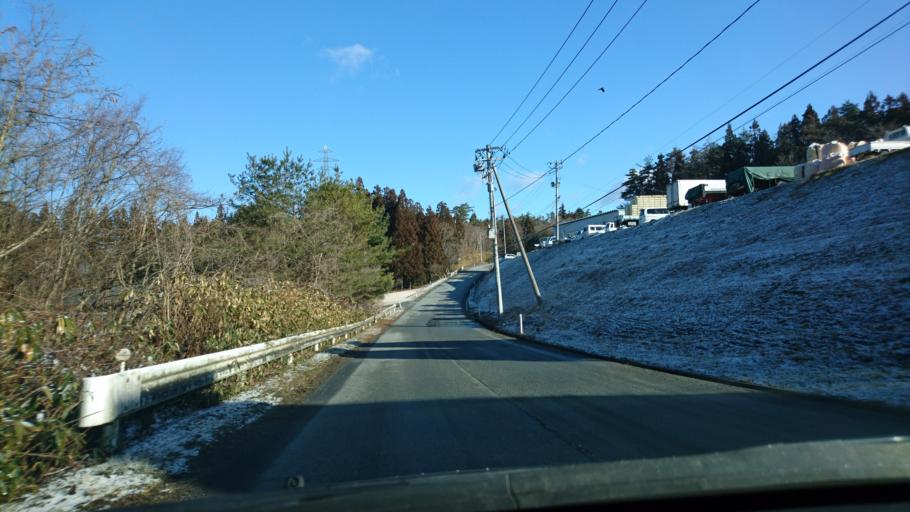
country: JP
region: Iwate
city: Ichinoseki
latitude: 38.8847
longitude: 141.3363
